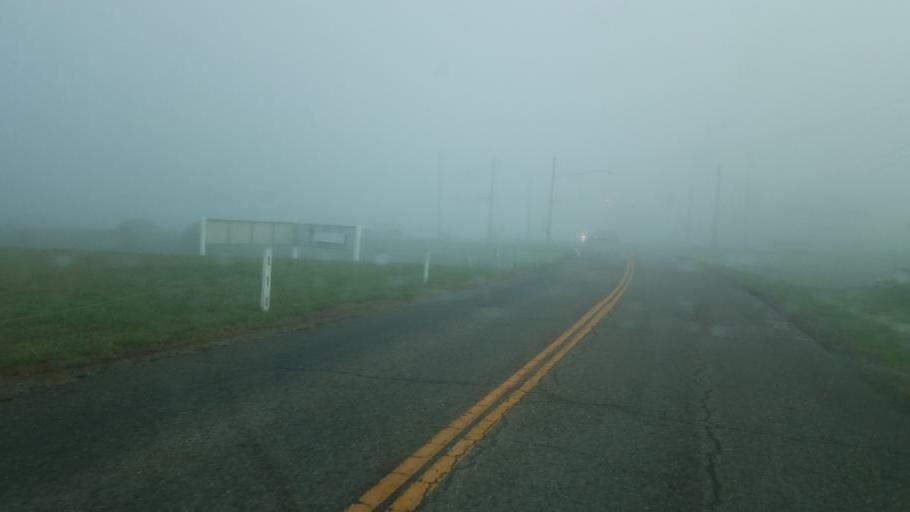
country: US
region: Ohio
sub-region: Tuscarawas County
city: Sugarcreek
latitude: 40.5088
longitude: -81.6100
